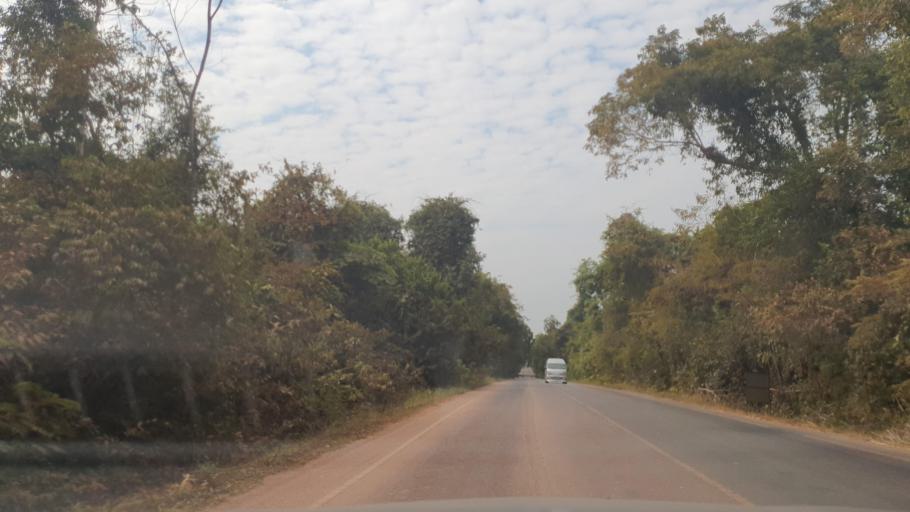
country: TH
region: Changwat Bueng Kan
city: Bung Khla
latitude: 18.3000
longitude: 103.9468
